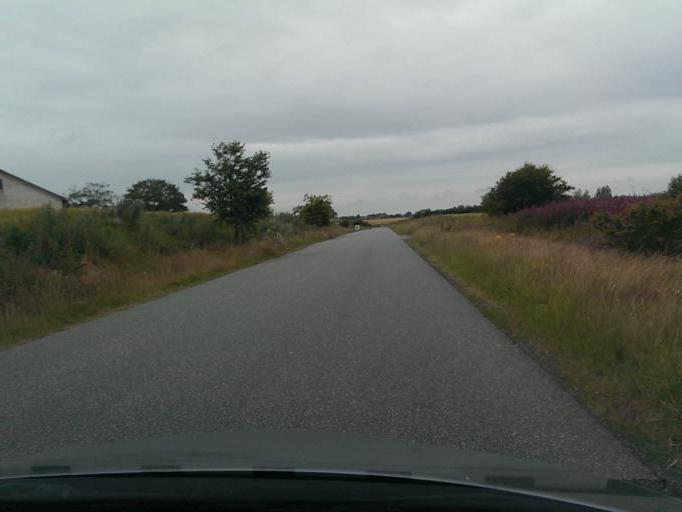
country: DK
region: North Denmark
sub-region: Hjorring Kommune
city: Vra
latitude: 57.3554
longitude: 9.9291
